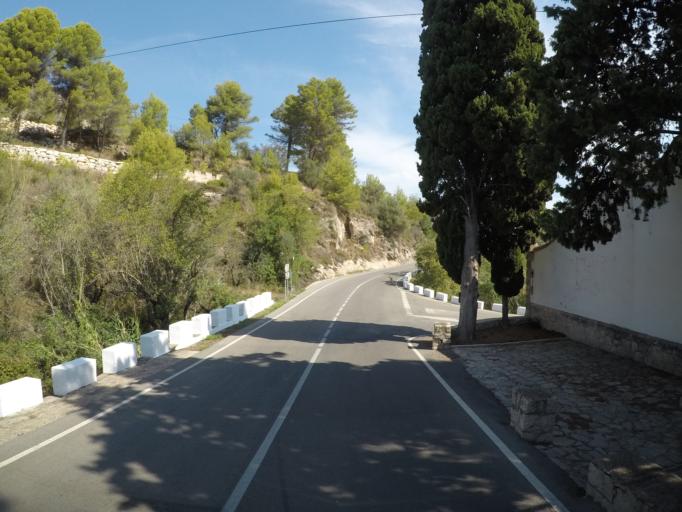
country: ES
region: Valencia
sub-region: Provincia de Alicante
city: Murla
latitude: 38.7803
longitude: -0.0960
